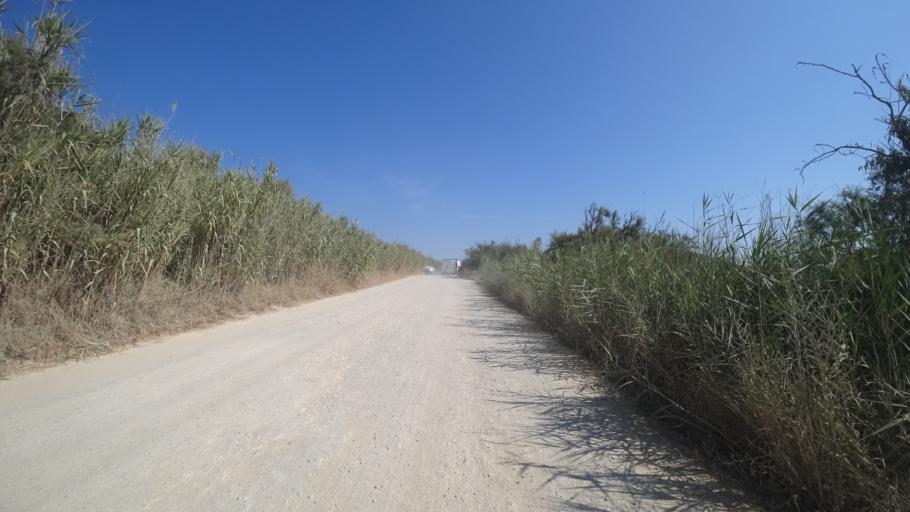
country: FR
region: Languedoc-Roussillon
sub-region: Departement des Pyrenees-Orientales
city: Le Barcares
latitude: 42.7712
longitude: 3.0356
